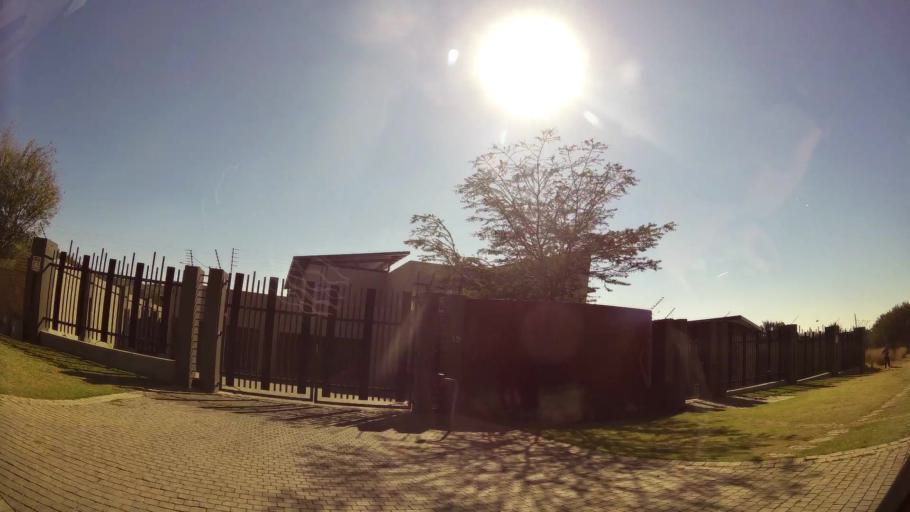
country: ZA
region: Gauteng
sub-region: Ekurhuleni Metropolitan Municipality
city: Germiston
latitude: -26.2881
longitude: 28.0984
